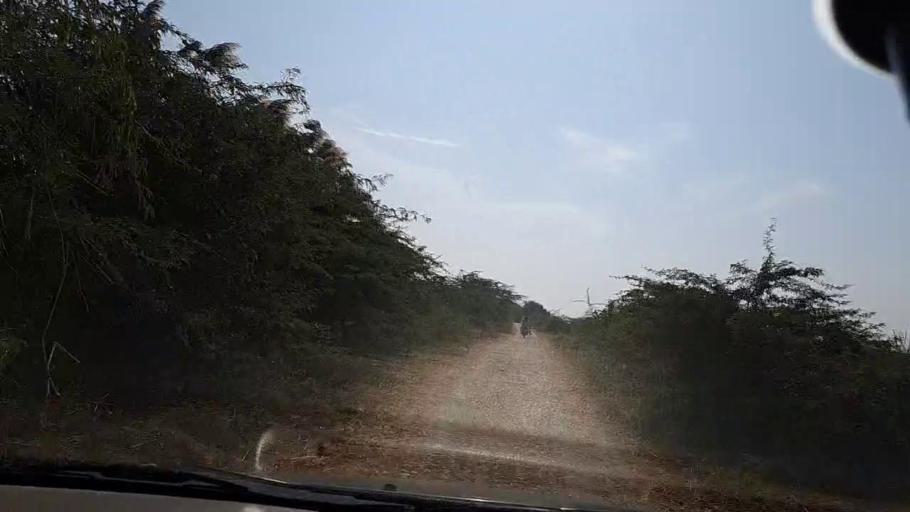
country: PK
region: Sindh
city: Mirpur Batoro
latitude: 24.6672
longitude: 68.2144
